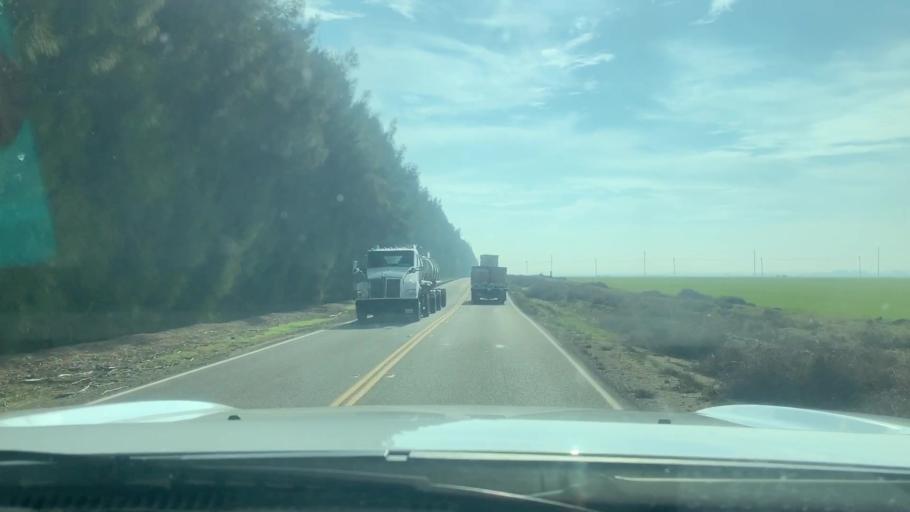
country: US
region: California
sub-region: Kern County
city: Lost Hills
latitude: 35.5042
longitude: -119.7433
